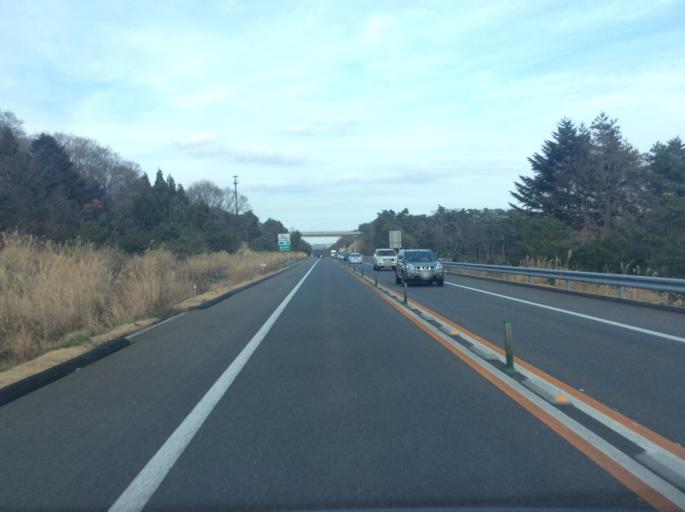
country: JP
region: Fukushima
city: Iwaki
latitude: 37.2415
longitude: 140.9856
